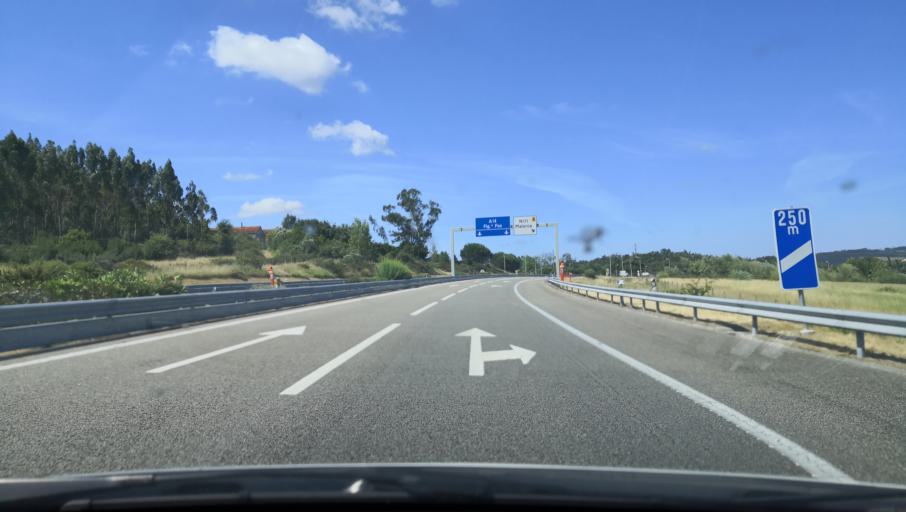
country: PT
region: Coimbra
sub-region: Montemor-O-Velho
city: Montemor-o-Velho
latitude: 40.1758
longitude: -8.7081
